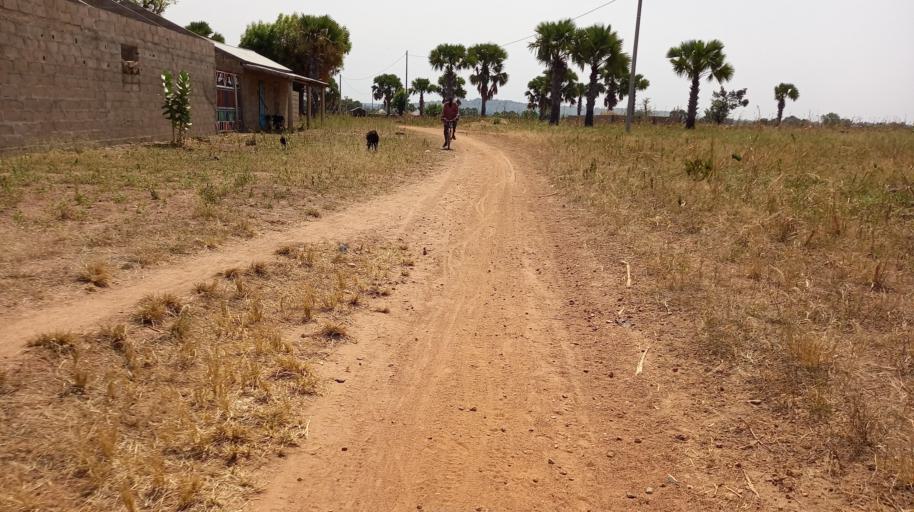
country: TG
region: Savanes
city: Dapaong
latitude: 10.9364
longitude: 0.3828
